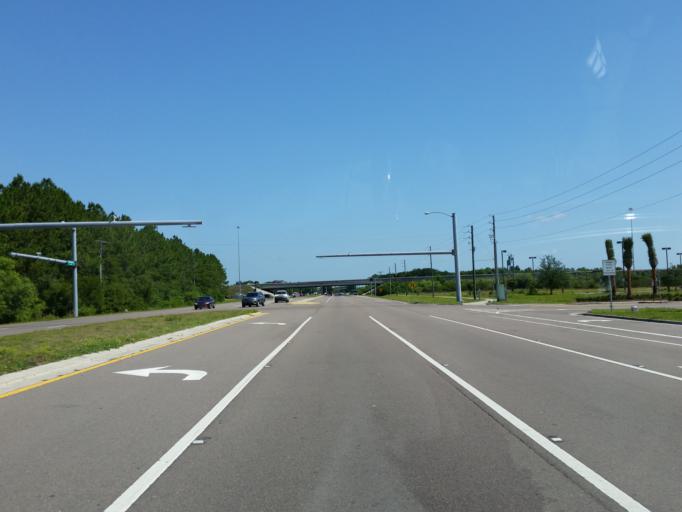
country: US
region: Florida
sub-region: Hillsborough County
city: Progress Village
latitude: 27.9247
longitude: -82.3380
